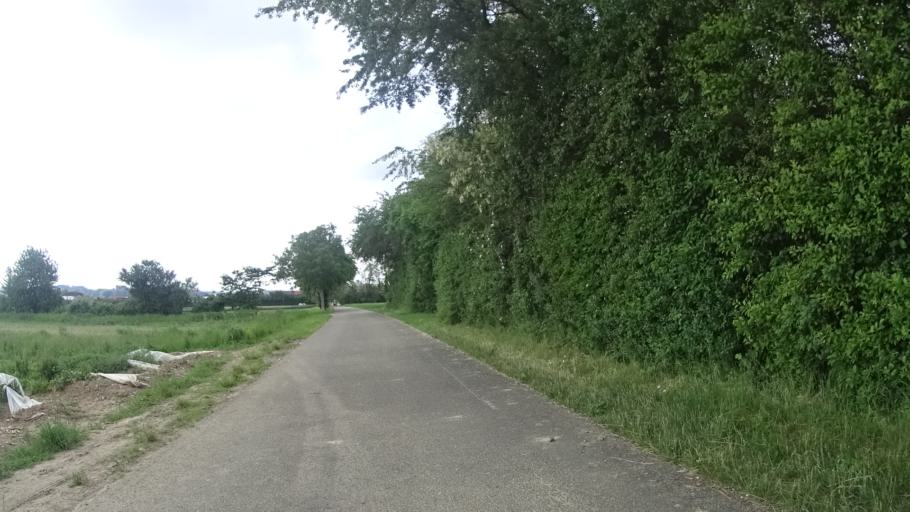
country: DE
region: Baden-Wuerttemberg
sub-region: Freiburg Region
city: Schliengen
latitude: 47.7763
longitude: 7.5529
